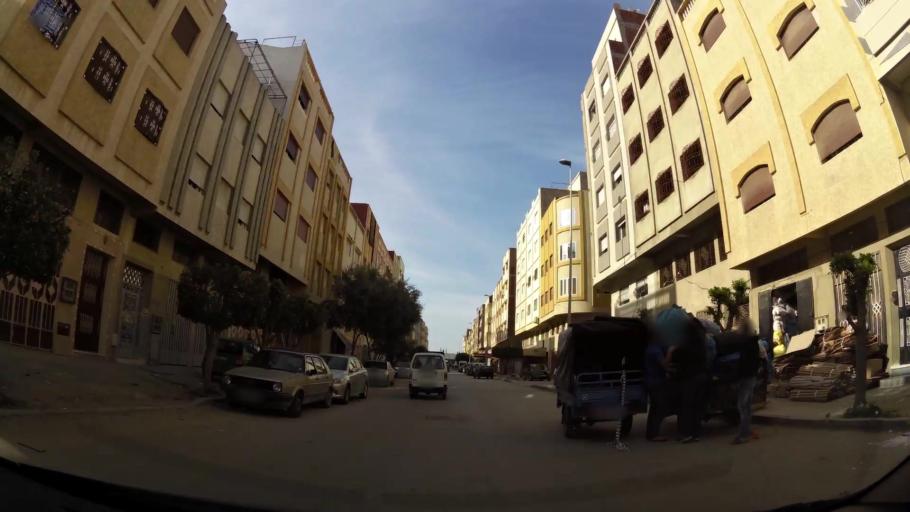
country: MA
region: Tanger-Tetouan
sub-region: Tanger-Assilah
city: Tangier
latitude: 35.7389
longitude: -5.7977
